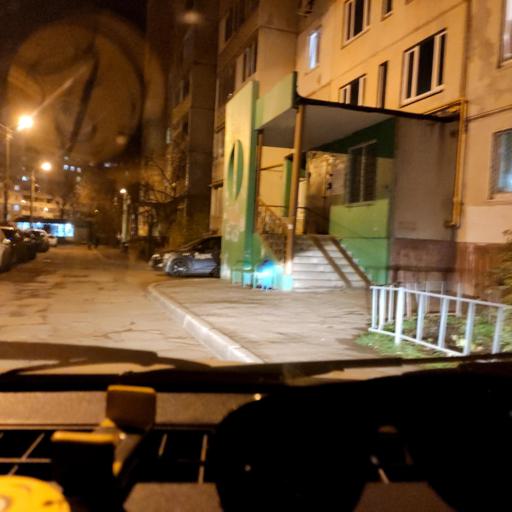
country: RU
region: Bashkortostan
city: Ufa
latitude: 54.7637
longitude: 56.0734
